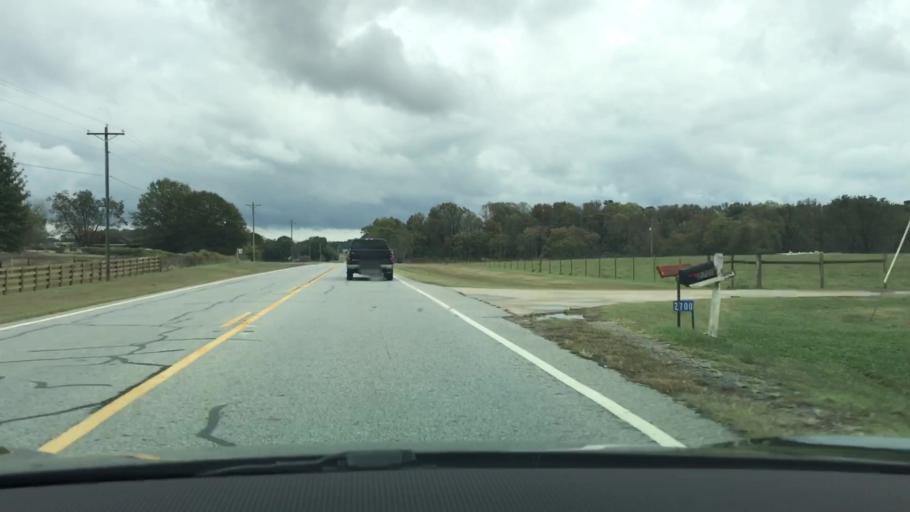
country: US
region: Georgia
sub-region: Oconee County
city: Watkinsville
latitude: 33.8255
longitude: -83.3719
